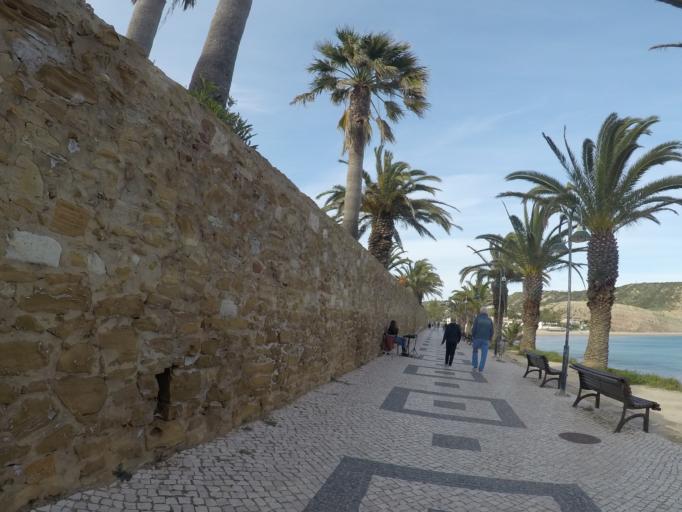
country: PT
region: Faro
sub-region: Lagos
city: Lagos
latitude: 37.0854
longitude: -8.7295
